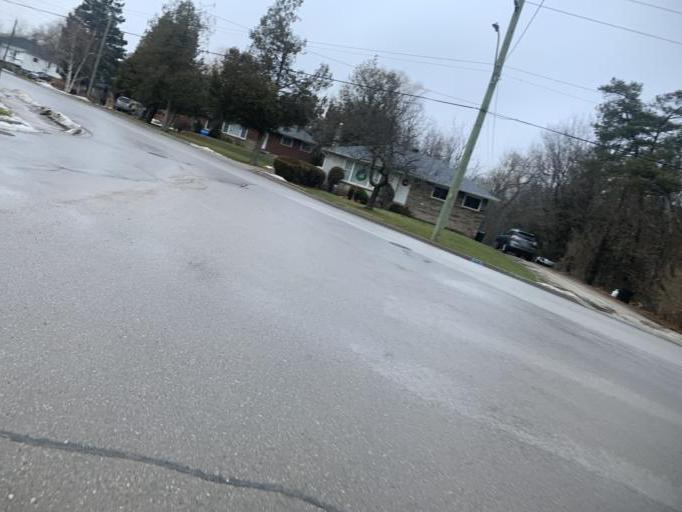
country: CA
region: Ontario
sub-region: Halton
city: Milton
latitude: 43.6562
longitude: -79.9275
